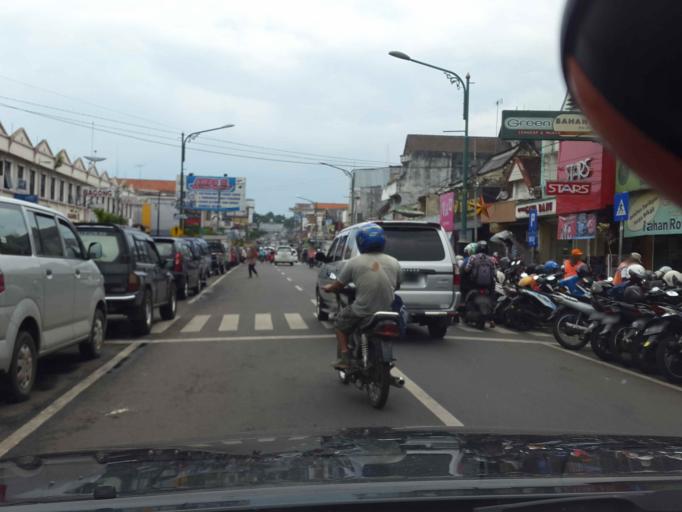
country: ID
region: Central Java
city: Salatiga
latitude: -7.3294
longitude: 110.5046
